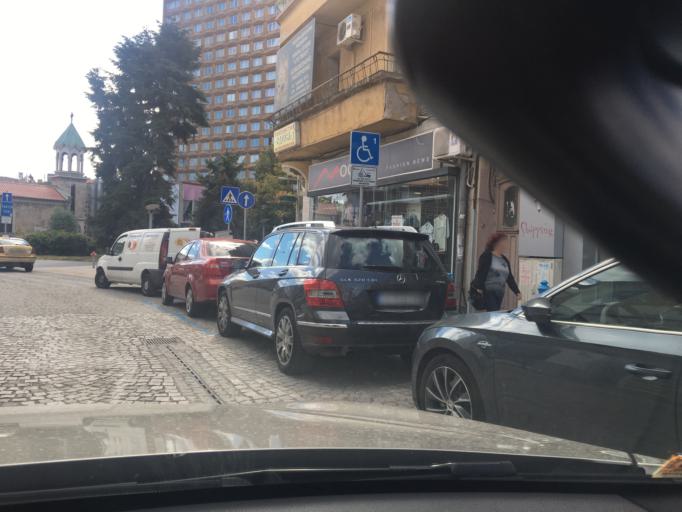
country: BG
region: Burgas
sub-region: Obshtina Burgas
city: Burgas
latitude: 42.4939
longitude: 27.4741
